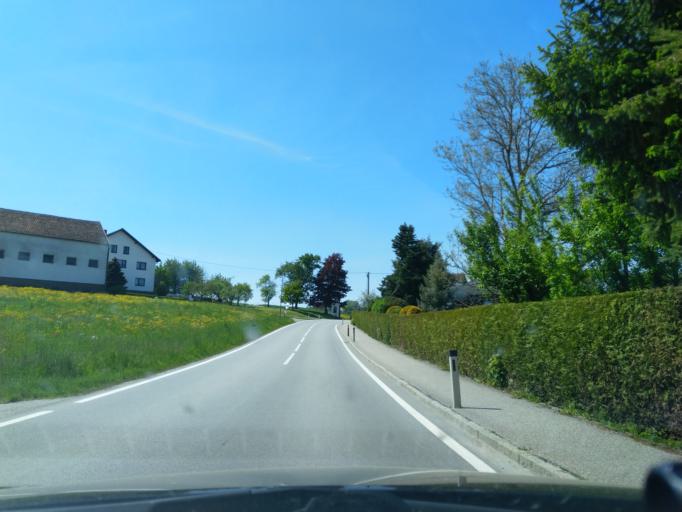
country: AT
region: Upper Austria
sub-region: Politischer Bezirk Ried im Innkreis
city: Ried im Innkreis
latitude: 48.2492
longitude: 13.4488
